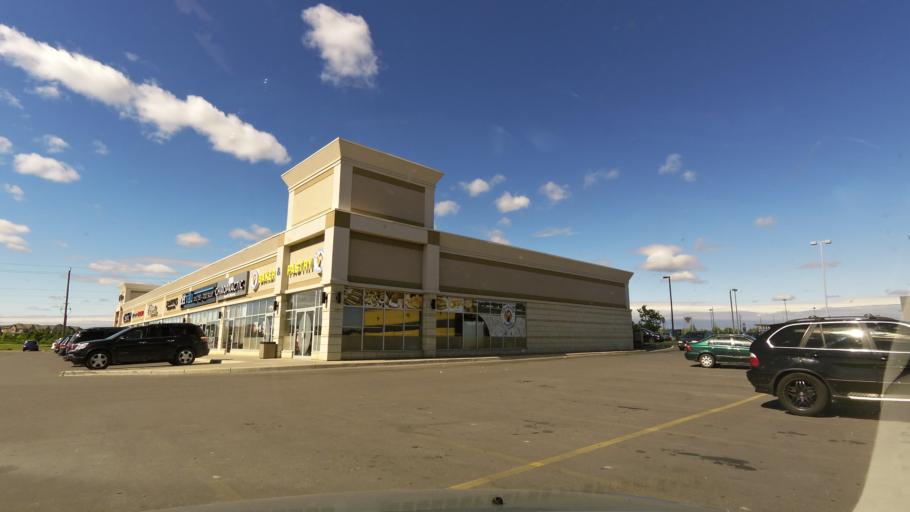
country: CA
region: Ontario
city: Bradford West Gwillimbury
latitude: 44.1087
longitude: -79.5854
